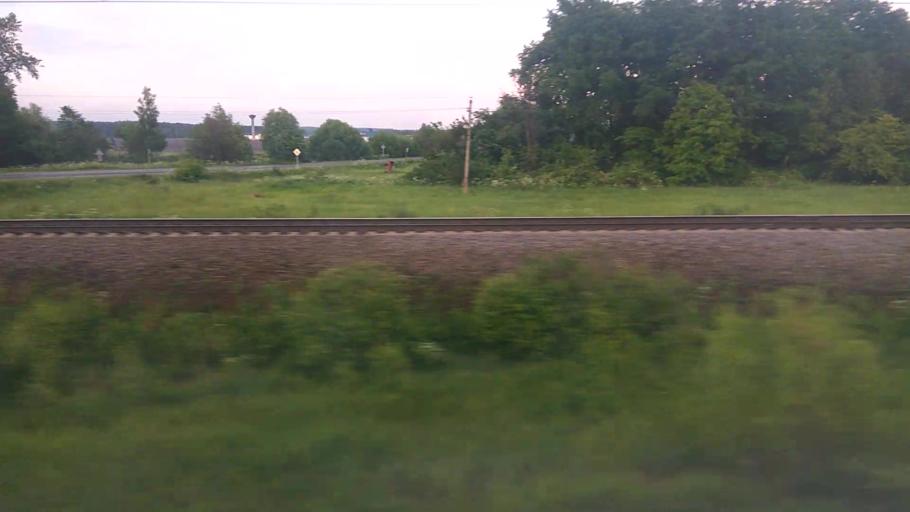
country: RU
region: Moskovskaya
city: Zhilevo
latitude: 55.0530
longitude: 37.9951
